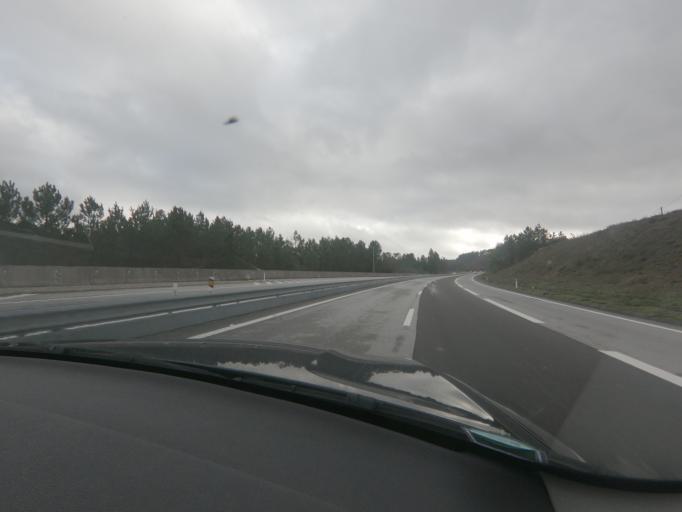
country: PT
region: Viseu
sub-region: Viseu
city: Campo
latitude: 40.7422
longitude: -7.9240
